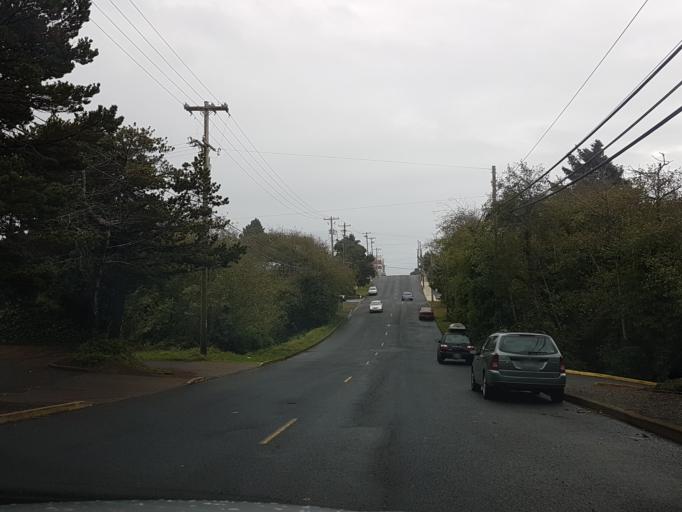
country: US
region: Oregon
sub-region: Lincoln County
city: Newport
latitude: 44.6396
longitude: -124.0557
